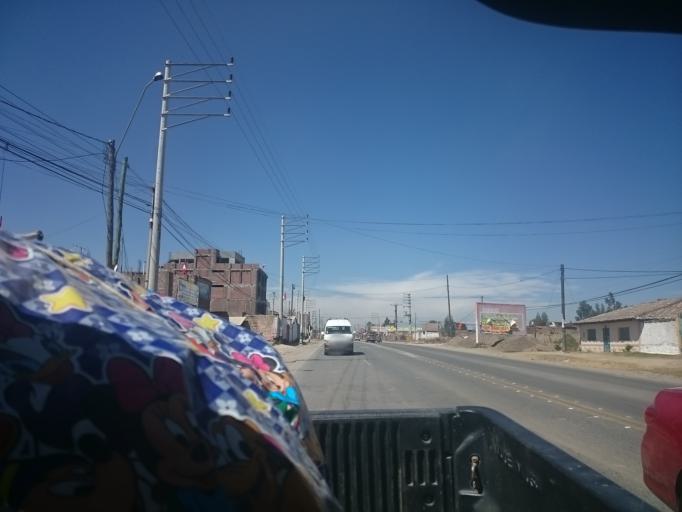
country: PE
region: Junin
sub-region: Provincia de Huancayo
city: Hualhuas
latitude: -12.0051
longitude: -75.2496
